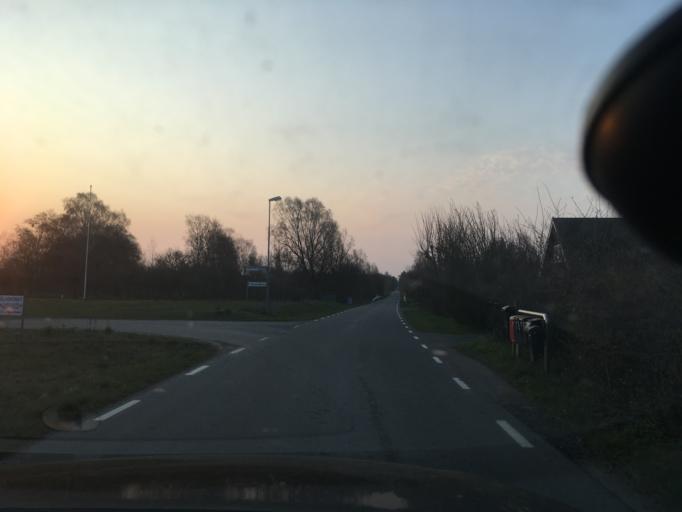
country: SE
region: Skane
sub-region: Ystads Kommun
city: Kopingebro
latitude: 55.4000
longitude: 14.1657
